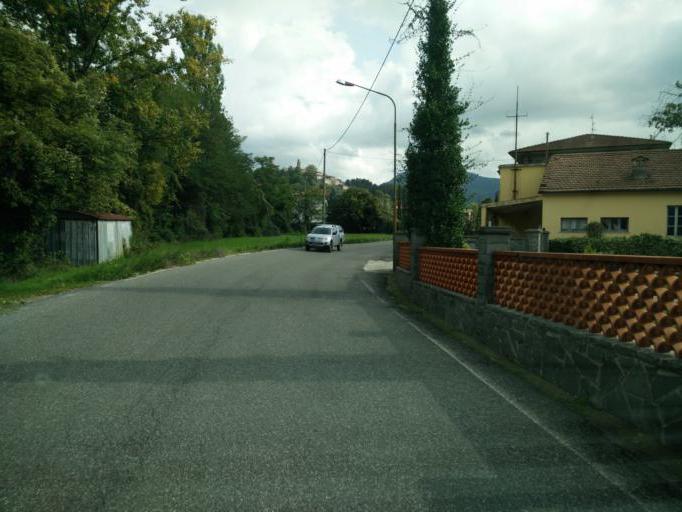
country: IT
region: Tuscany
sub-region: Provincia di Massa-Carrara
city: Villafranca in Lunigiana
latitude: 44.3136
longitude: 9.9624
